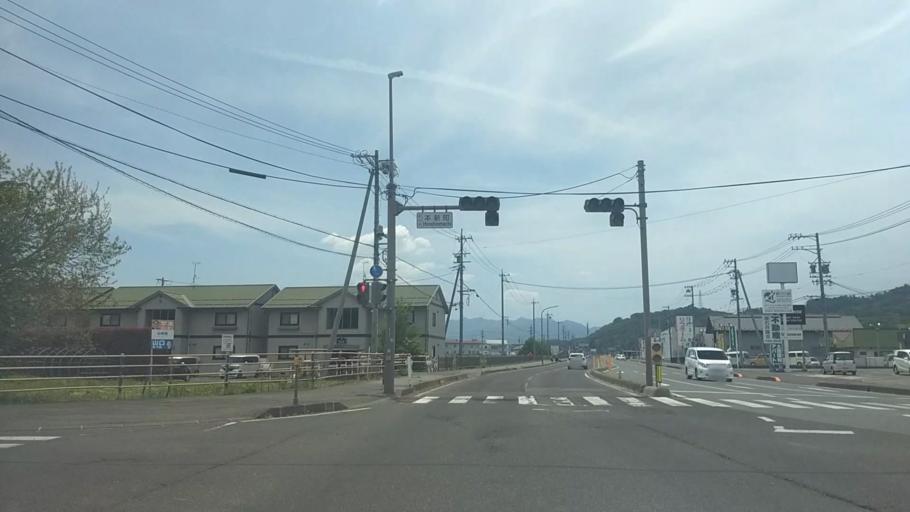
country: JP
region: Nagano
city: Saku
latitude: 36.2122
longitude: 138.4650
